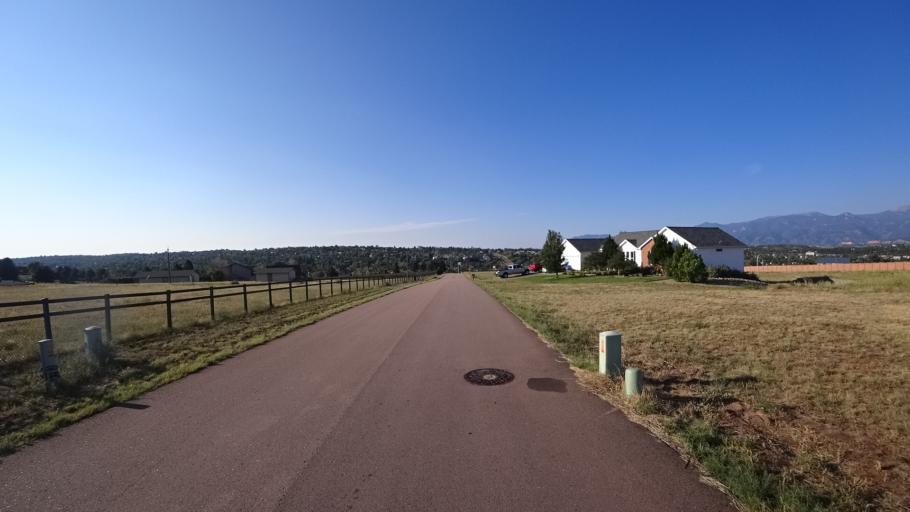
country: US
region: Colorado
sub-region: El Paso County
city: Air Force Academy
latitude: 38.9351
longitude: -104.7748
